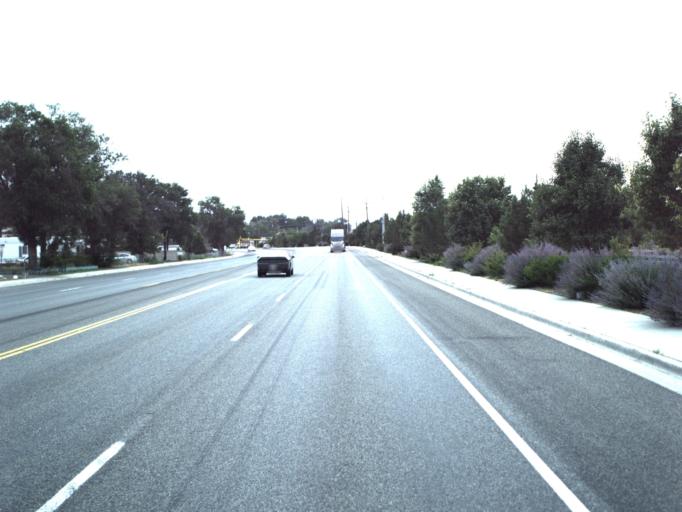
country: US
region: Utah
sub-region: Carbon County
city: Wellington
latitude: 39.5431
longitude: -110.7411
